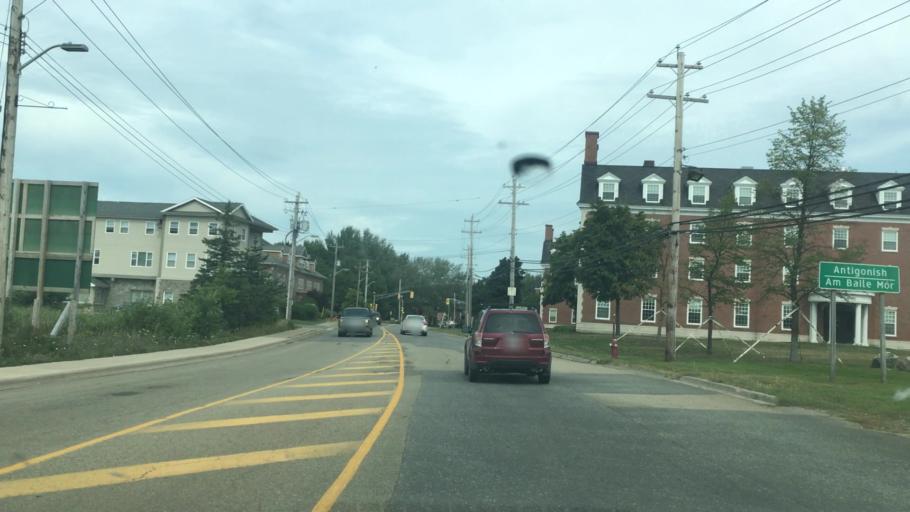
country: CA
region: Nova Scotia
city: Antigonish
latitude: 45.6148
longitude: -61.9986
